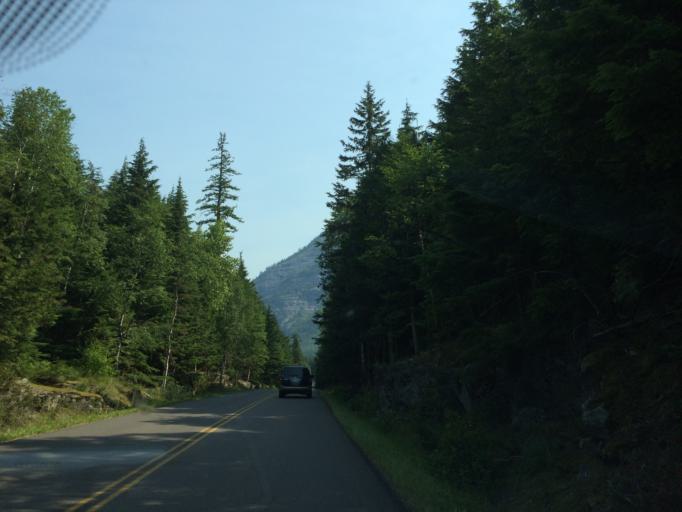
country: US
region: Montana
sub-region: Flathead County
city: Columbia Falls
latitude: 48.6654
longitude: -113.8331
